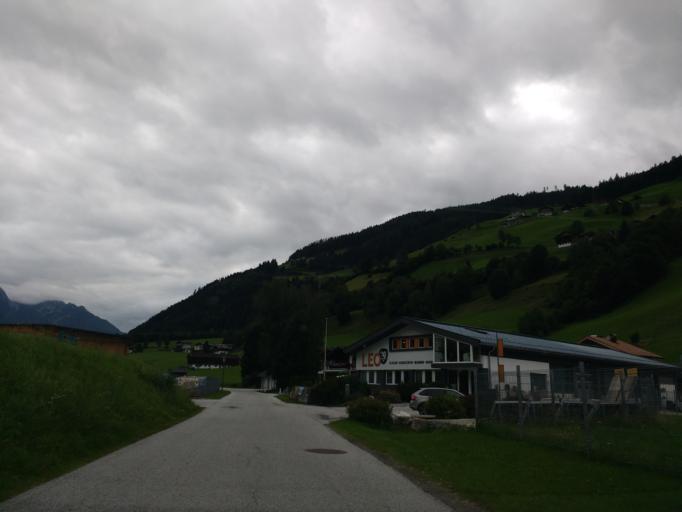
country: AT
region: Salzburg
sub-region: Politischer Bezirk Zell am See
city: Bramberg am Wildkogel
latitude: 47.2662
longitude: 12.3325
